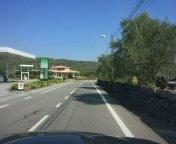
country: PT
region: Viseu
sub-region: Sernancelhe
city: Sernancelhe
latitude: 40.9253
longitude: -7.5085
